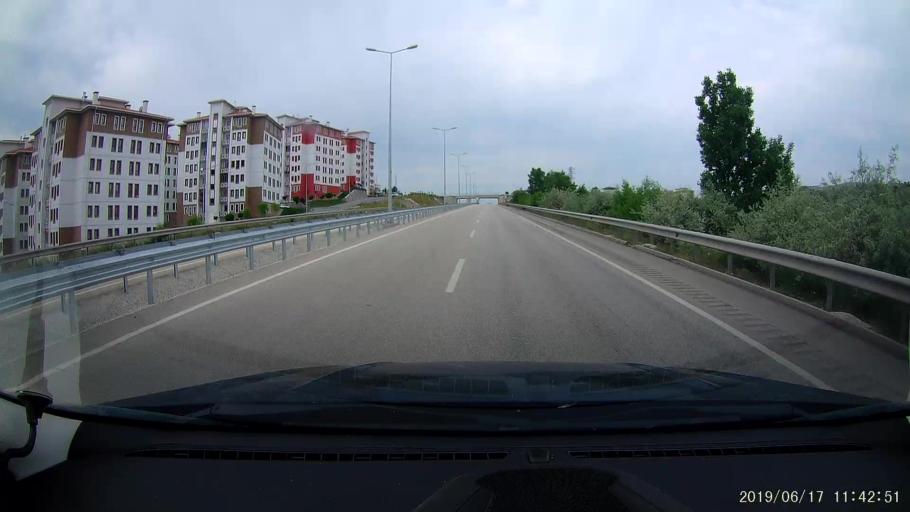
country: TR
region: Cankiri
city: Kursunlu
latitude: 40.8384
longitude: 33.2909
